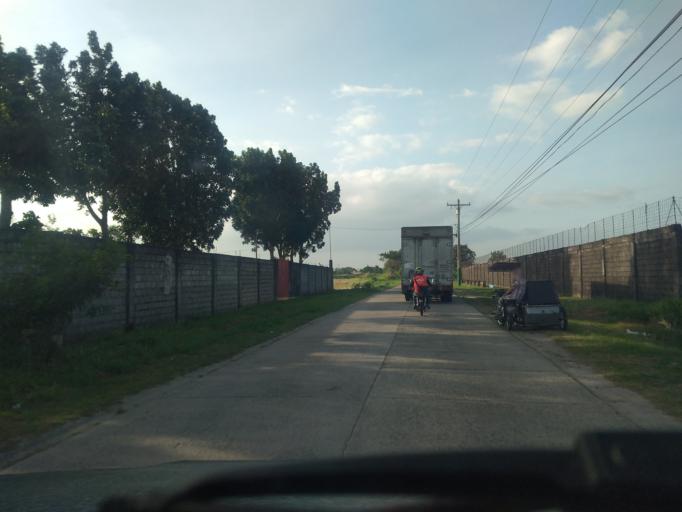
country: PH
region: Central Luzon
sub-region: Province of Pampanga
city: Malino
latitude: 15.1085
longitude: 120.6694
